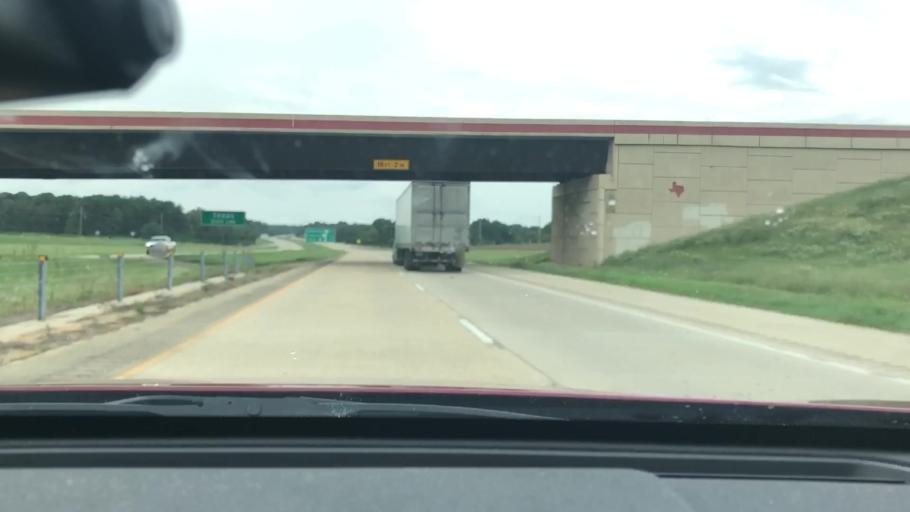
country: US
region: Texas
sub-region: Bowie County
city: Texarkana
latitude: 33.3858
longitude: -94.0429
